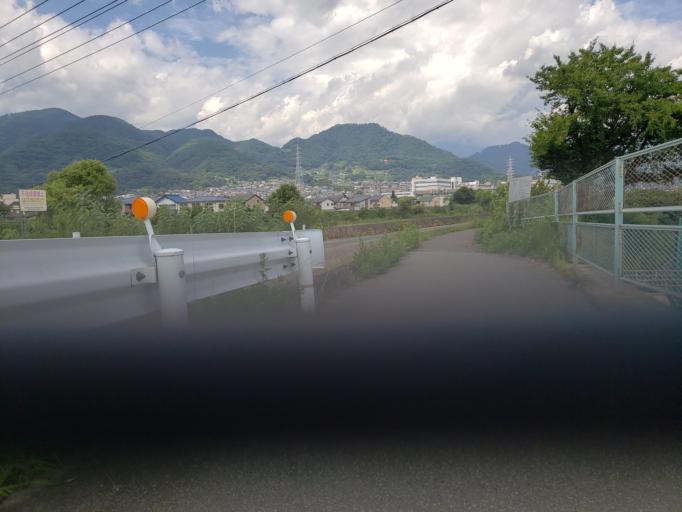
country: JP
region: Nagano
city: Nagano-shi
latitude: 36.6324
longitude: 138.1797
